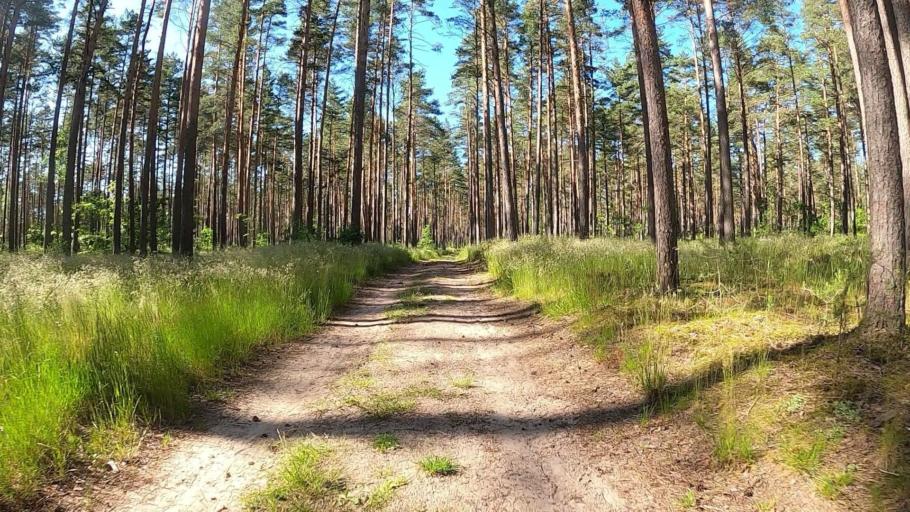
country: LV
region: Riga
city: Bergi
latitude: 57.0144
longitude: 24.2536
